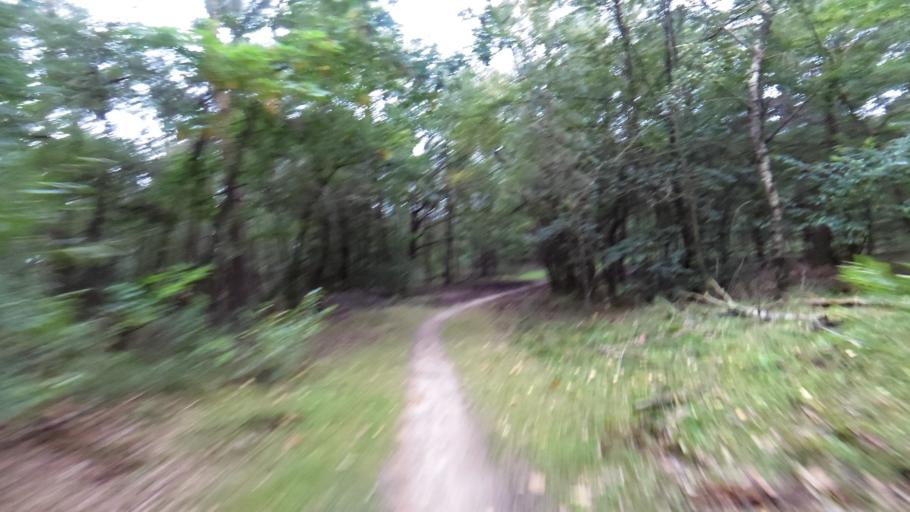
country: NL
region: Gelderland
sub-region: Gemeente Ede
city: Harskamp
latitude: 52.1729
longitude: 5.8365
